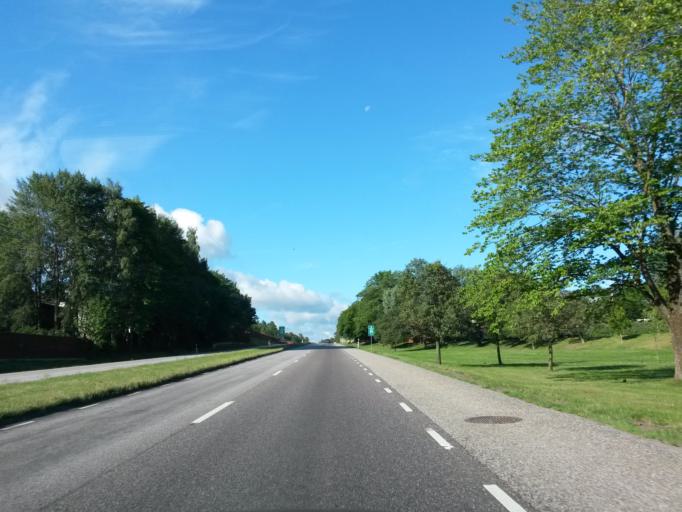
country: SE
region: Vaestra Goetaland
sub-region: Alingsas Kommun
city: Alingsas
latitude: 57.9220
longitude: 12.5248
